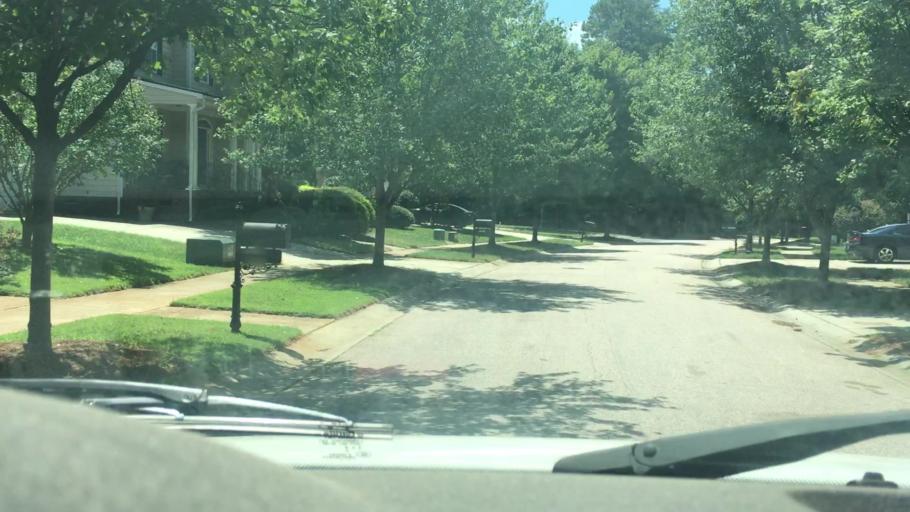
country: US
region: North Carolina
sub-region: Mecklenburg County
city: Cornelius
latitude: 35.4629
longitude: -80.8608
